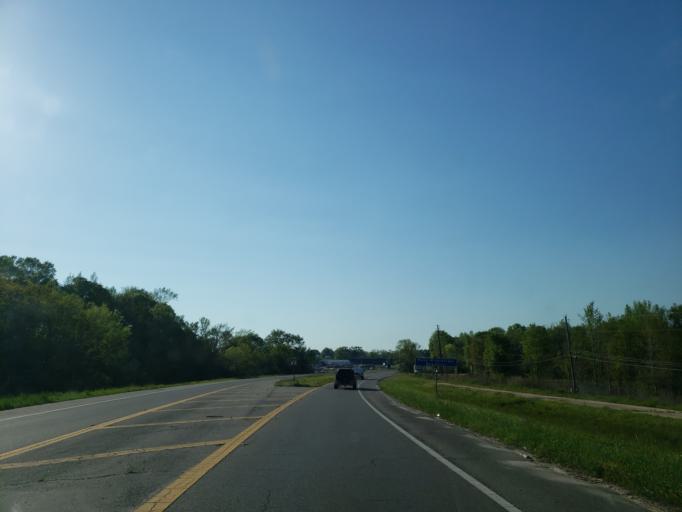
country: US
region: Mississippi
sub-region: Jones County
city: Laurel
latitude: 31.6829
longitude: -89.1200
